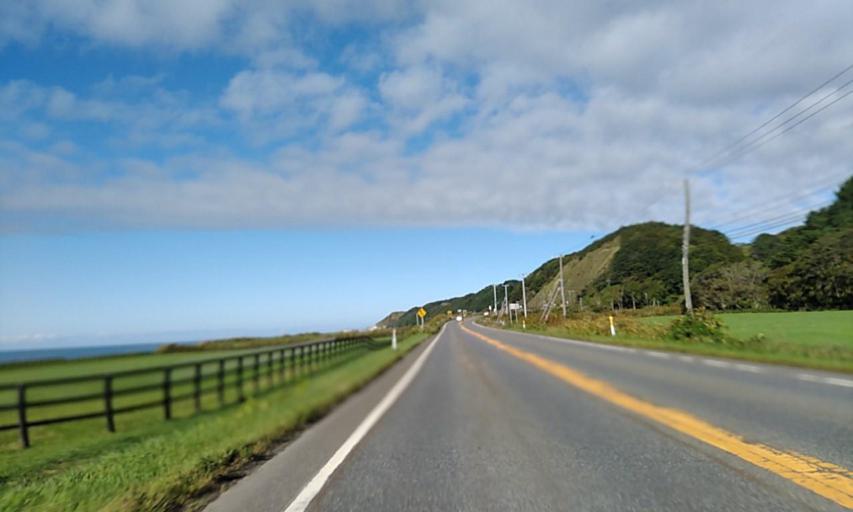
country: JP
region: Hokkaido
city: Shizunai-furukawacho
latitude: 42.3095
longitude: 142.4300
